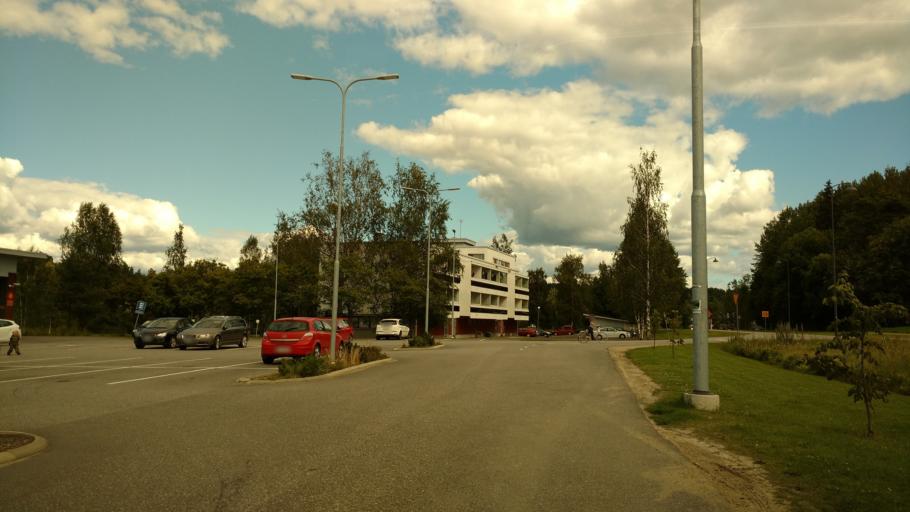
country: FI
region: Varsinais-Suomi
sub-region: Salo
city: Pernioe
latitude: 60.2055
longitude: 23.1138
